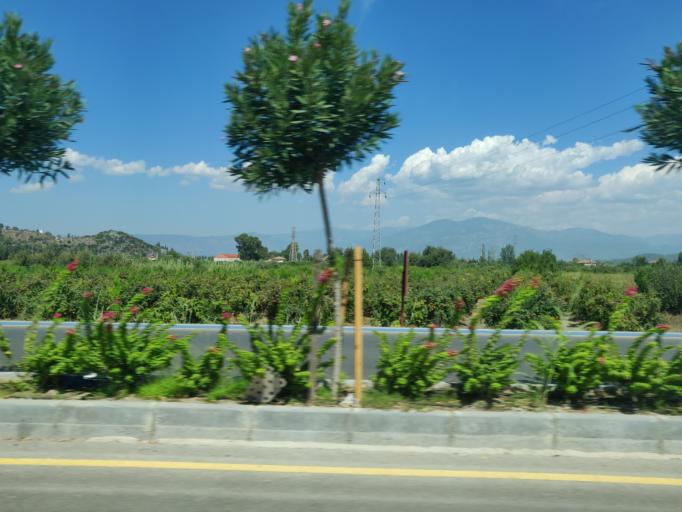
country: TR
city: Dalyan
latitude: 36.8406
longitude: 28.6547
